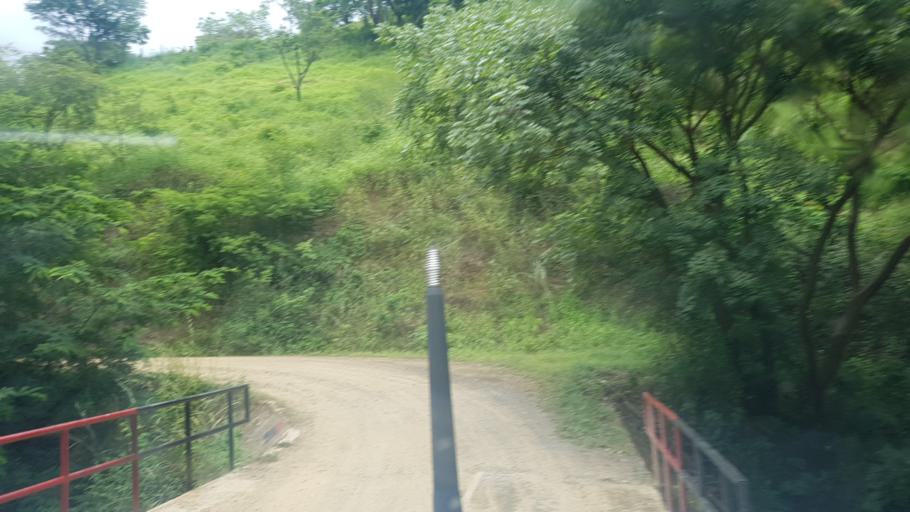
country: HN
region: El Paraiso
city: Oropoli
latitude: 13.7394
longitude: -86.7009
